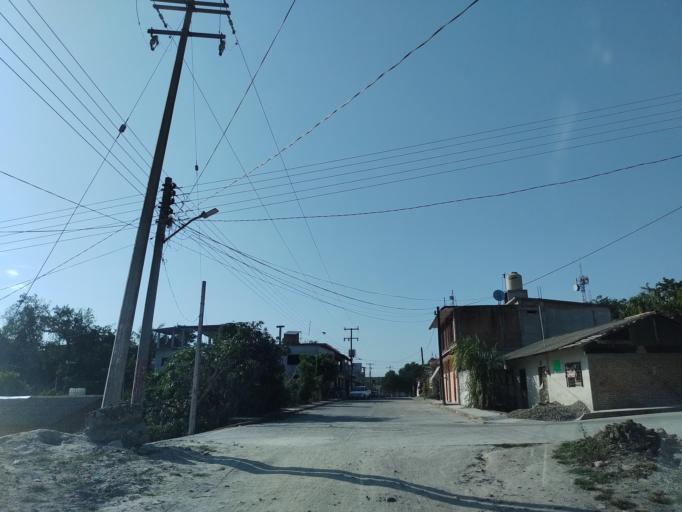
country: MX
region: Veracruz
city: Agua Dulce
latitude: 20.2531
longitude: -97.2542
